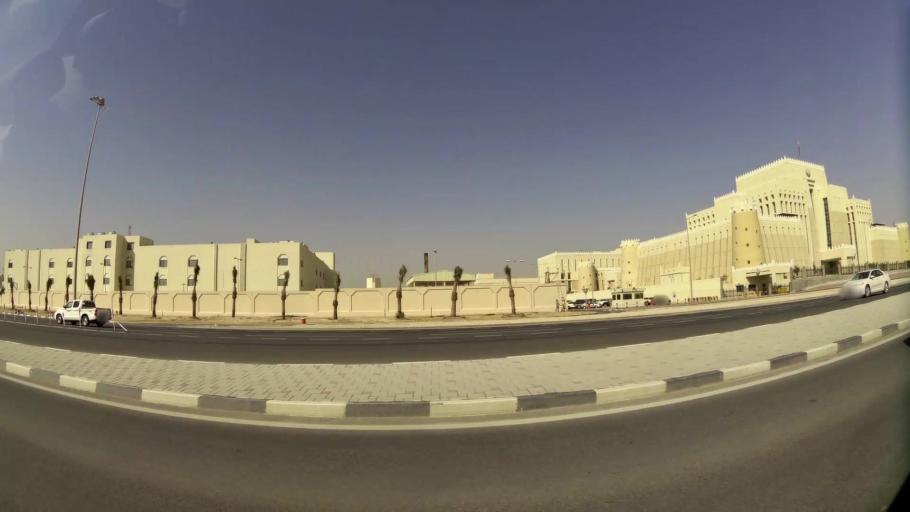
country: QA
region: Baladiyat ad Dawhah
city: Doha
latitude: 25.3045
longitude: 51.5064
